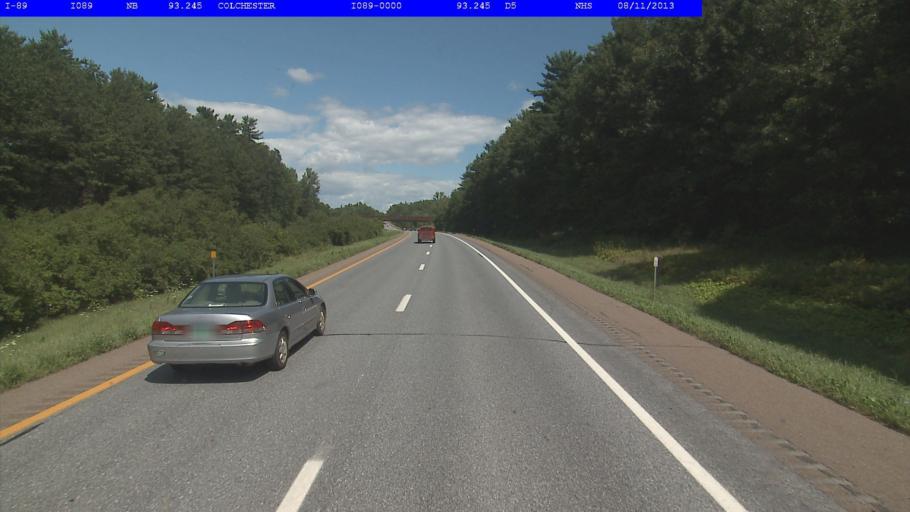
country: US
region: Vermont
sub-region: Chittenden County
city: Winooski
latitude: 44.5275
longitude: -73.1938
